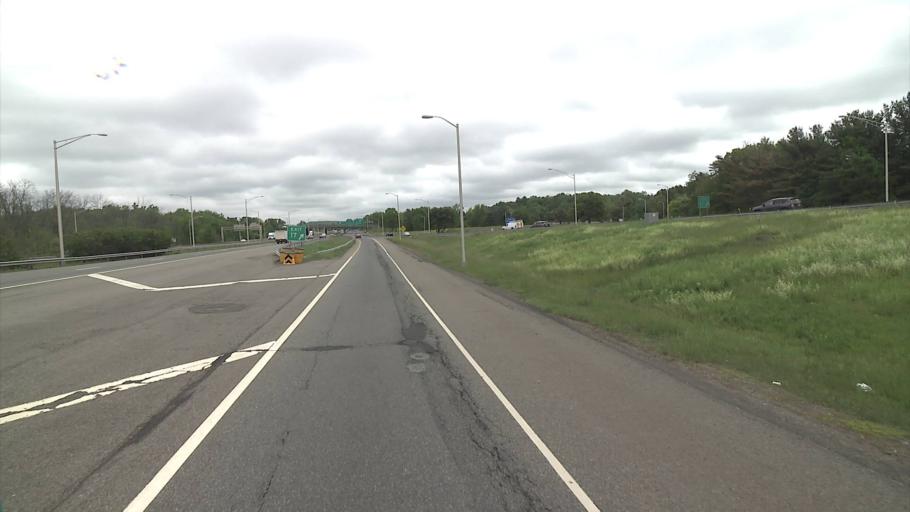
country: US
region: Connecticut
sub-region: New Haven County
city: Meriden
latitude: 41.5225
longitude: -72.7709
